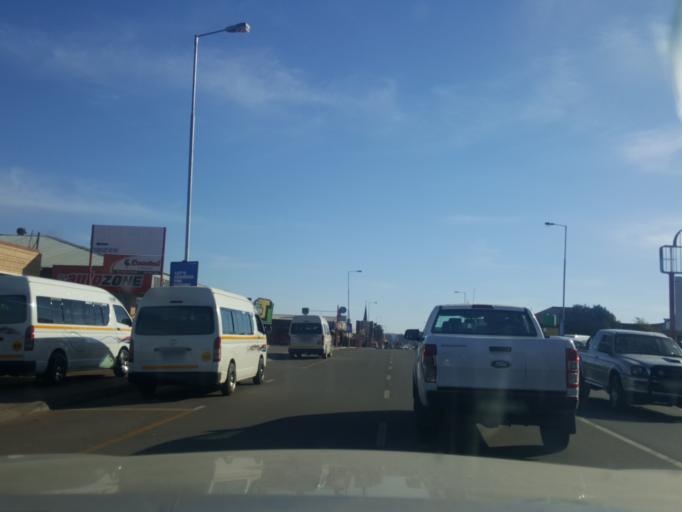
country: ZA
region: North-West
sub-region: Ngaka Modiri Molema District Municipality
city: Zeerust
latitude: -25.5436
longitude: 26.0858
